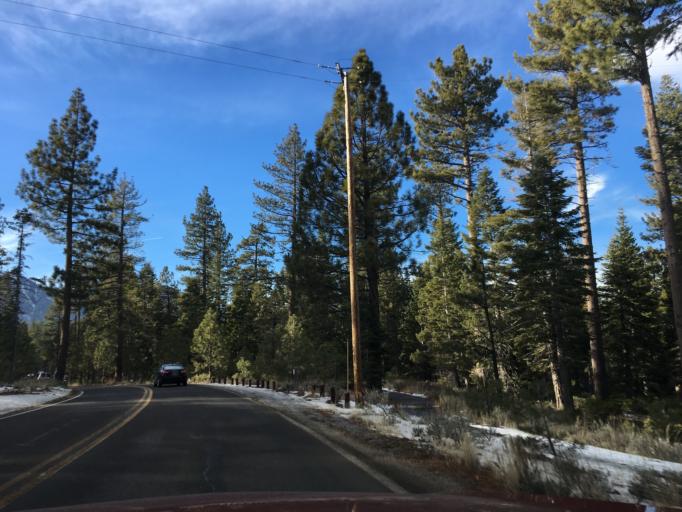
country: US
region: California
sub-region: El Dorado County
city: South Lake Tahoe
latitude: 38.9337
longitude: -120.0600
